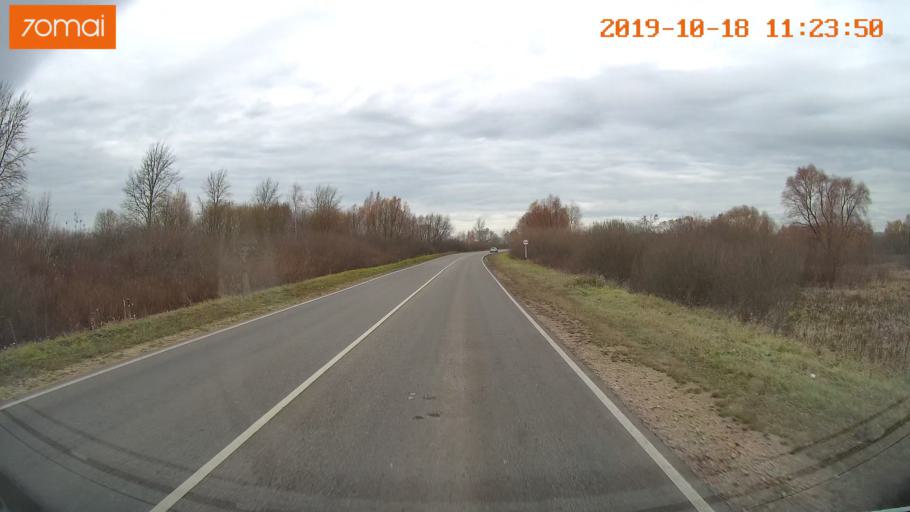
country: RU
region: Tula
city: Kimovsk
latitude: 54.1074
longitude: 38.5945
